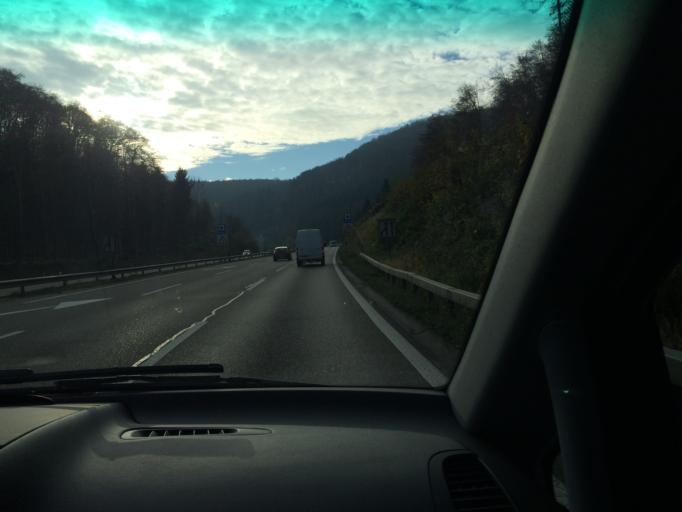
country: CH
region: Basel-Landschaft
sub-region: Bezirk Liestal
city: Arisdorf
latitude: 47.4934
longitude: 7.7708
